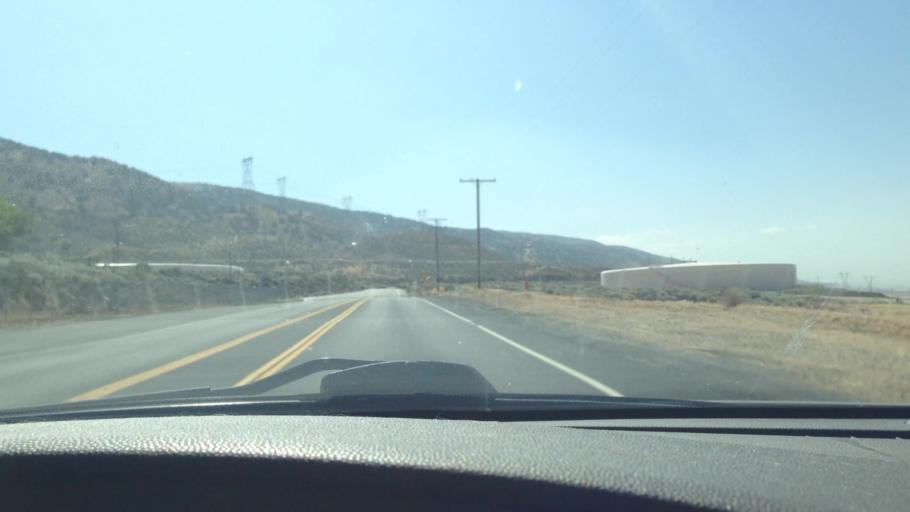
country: US
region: California
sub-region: Los Angeles County
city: Quartz Hill
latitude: 34.6308
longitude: -118.2440
